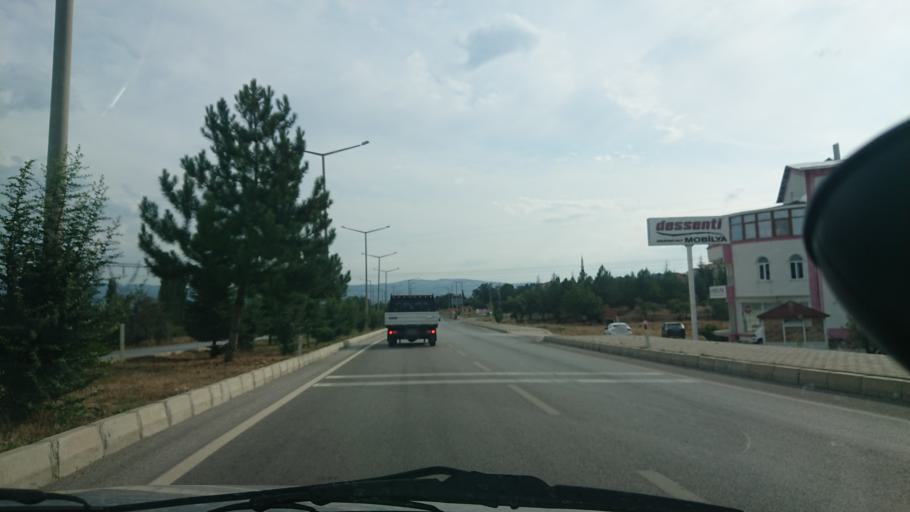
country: TR
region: Kuetahya
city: Gediz
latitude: 39.0016
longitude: 29.4041
